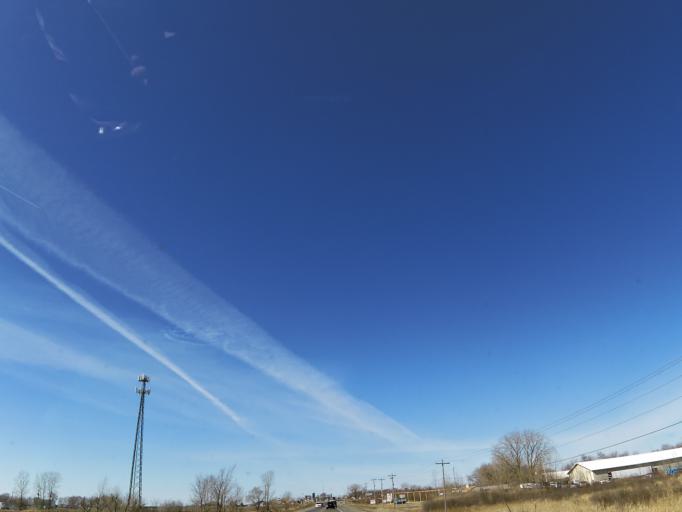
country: US
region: Minnesota
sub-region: Hennepin County
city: Medina
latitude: 45.0655
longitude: -93.6267
